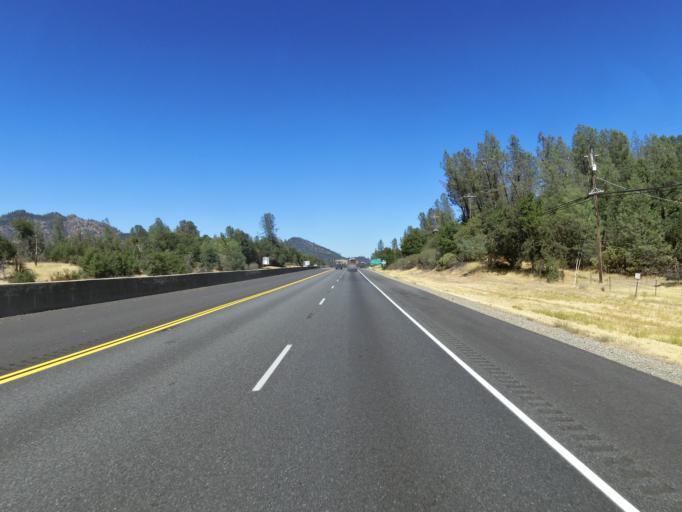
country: US
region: California
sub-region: Shasta County
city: Shasta Lake
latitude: 40.6898
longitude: -122.3454
